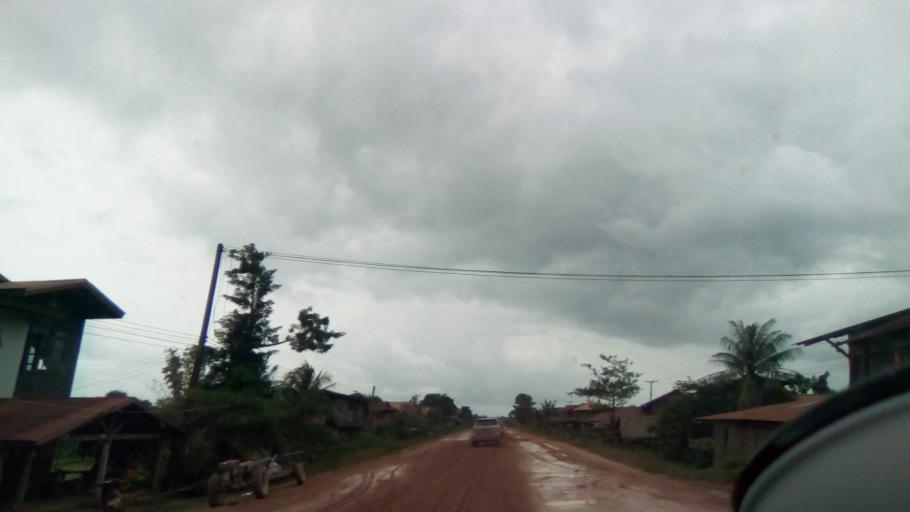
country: LA
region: Attapu
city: Attapu
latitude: 14.7409
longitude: 106.6906
